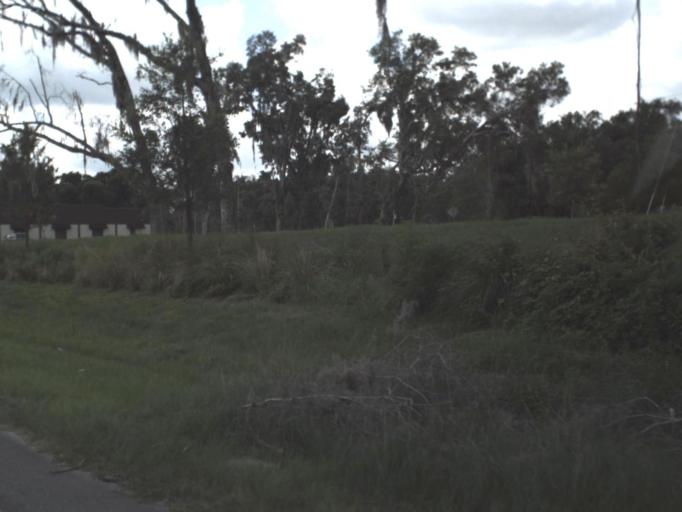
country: US
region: Florida
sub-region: Hernando County
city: Brooksville
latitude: 28.5803
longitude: -82.3756
